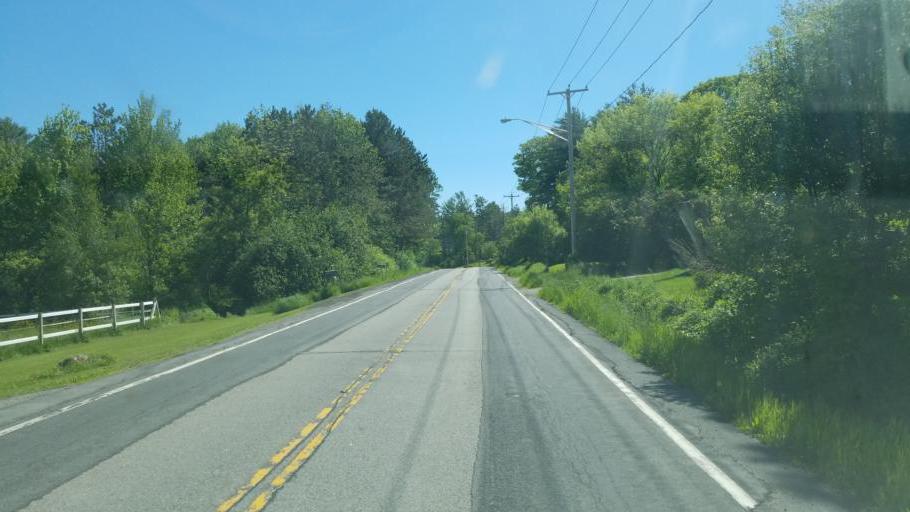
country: US
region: New York
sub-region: Montgomery County
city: Canajoharie
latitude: 43.0402
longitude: -74.5278
